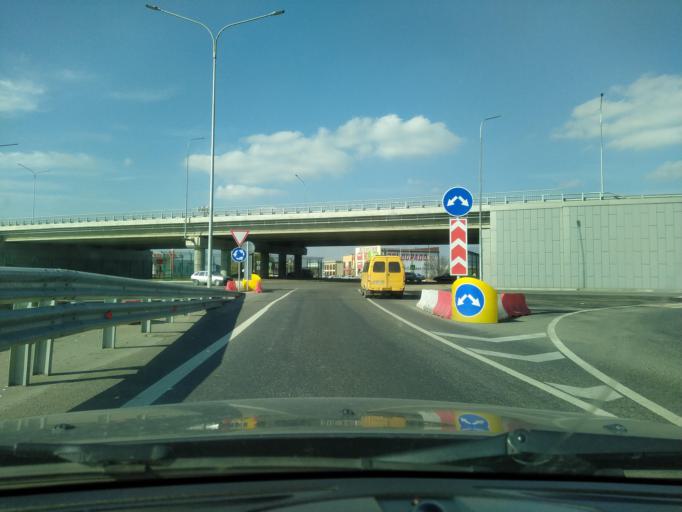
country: RU
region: Ingushetiya
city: Magas
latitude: 43.1949
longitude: 44.7618
